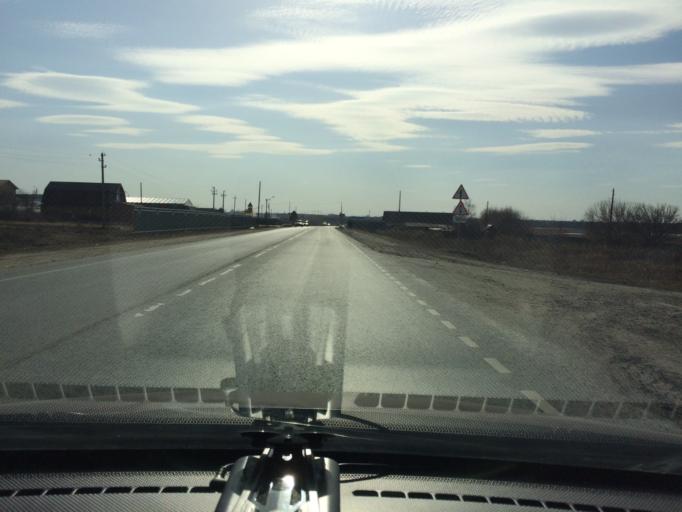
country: RU
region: Mariy-El
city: Yoshkar-Ola
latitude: 56.6602
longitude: 47.9743
